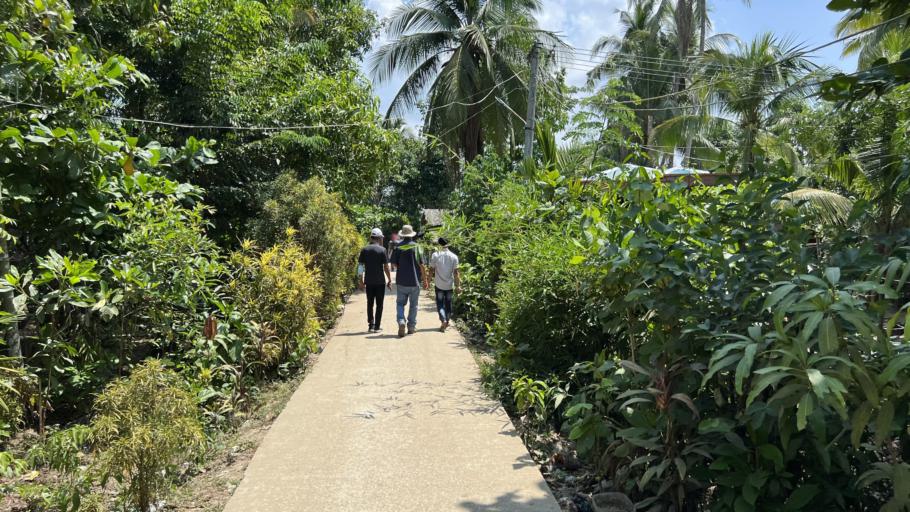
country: MM
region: Ayeyarwady
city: Kyaiklat
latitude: 16.4158
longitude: 95.8786
